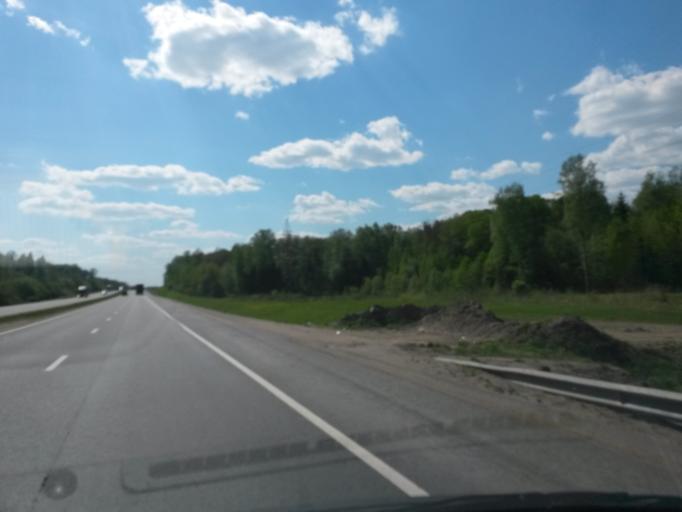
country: RU
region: Jaroslavl
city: Krasnyye Tkachi
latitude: 57.4011
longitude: 39.6492
